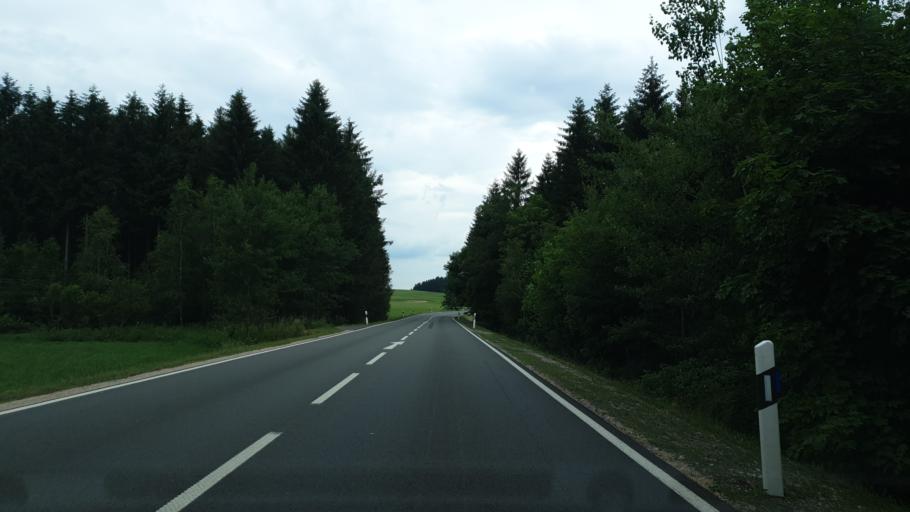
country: DE
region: Saxony
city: Waldkirchen
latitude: 50.6006
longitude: 12.4121
